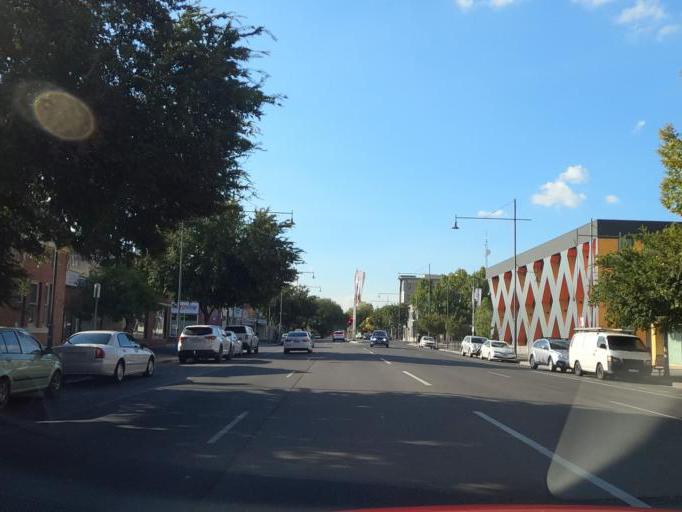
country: AU
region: New South Wales
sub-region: Albury Municipality
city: Albury
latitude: -36.0798
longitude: 146.9158
